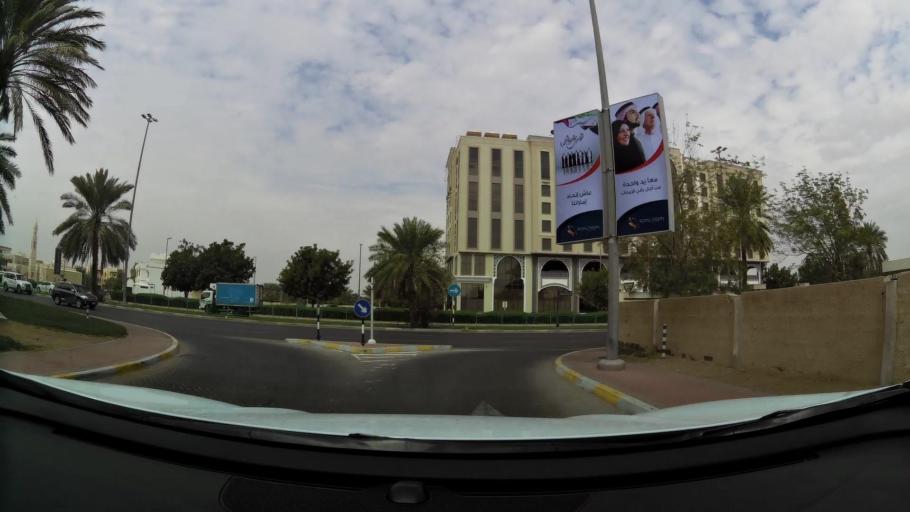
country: OM
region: Al Buraimi
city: Al Buraymi
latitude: 24.2236
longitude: 55.7831
